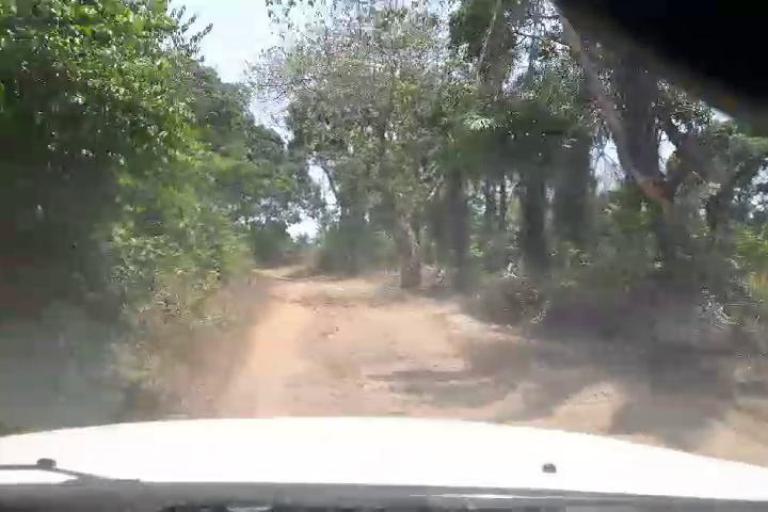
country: SL
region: Northern Province
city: Alikalia
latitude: 9.0721
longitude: -11.4829
